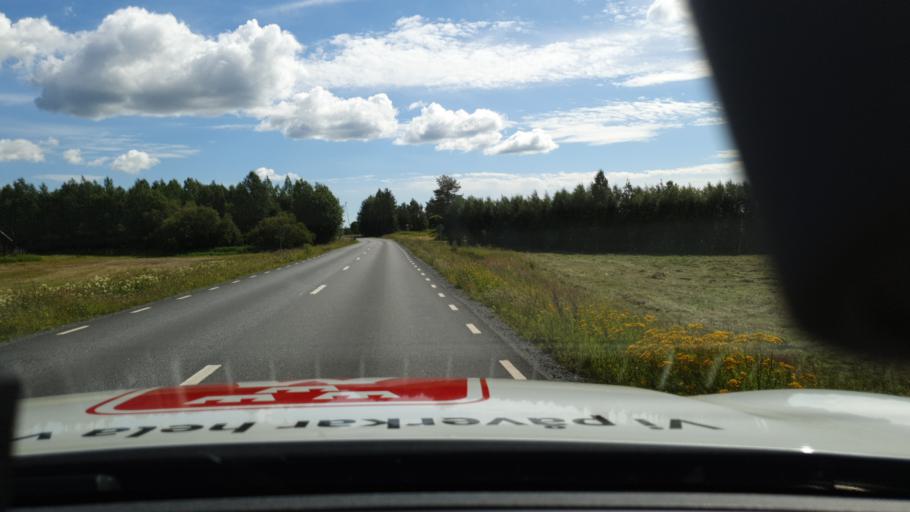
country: SE
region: Norrbotten
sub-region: Lulea Kommun
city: Gammelstad
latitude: 65.8047
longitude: 22.0340
